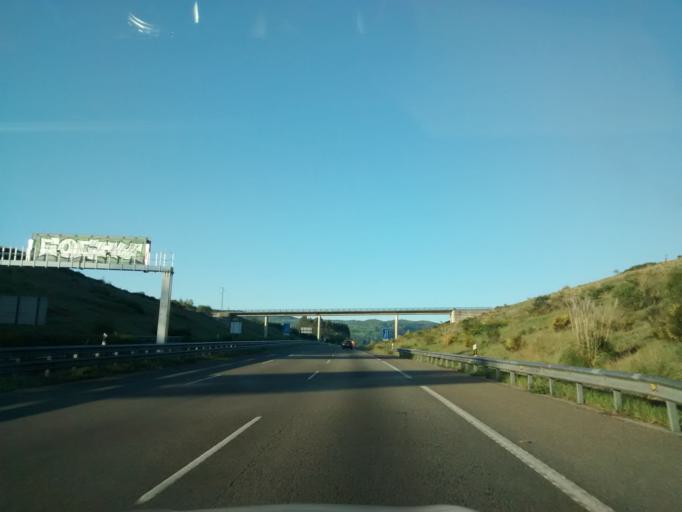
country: ES
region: Asturias
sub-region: Province of Asturias
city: Villaviciosa
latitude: 43.4822
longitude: -5.4579
